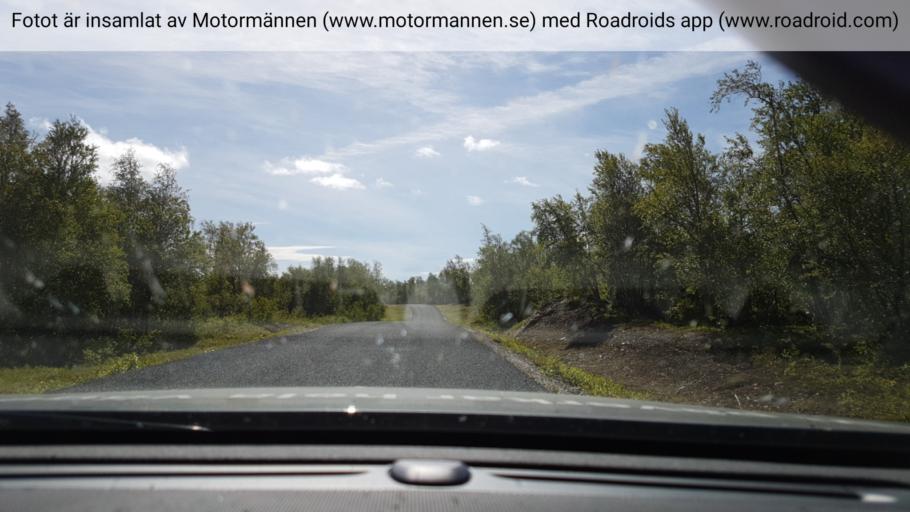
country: NO
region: Nordland
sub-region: Hattfjelldal
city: Hattfjelldal
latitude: 65.4127
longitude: 14.9323
